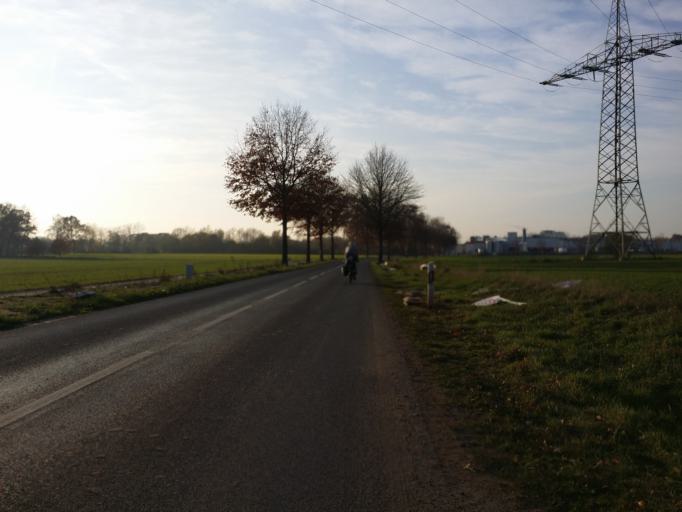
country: DE
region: Lower Saxony
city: Ottersberg
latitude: 53.1204
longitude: 9.1504
